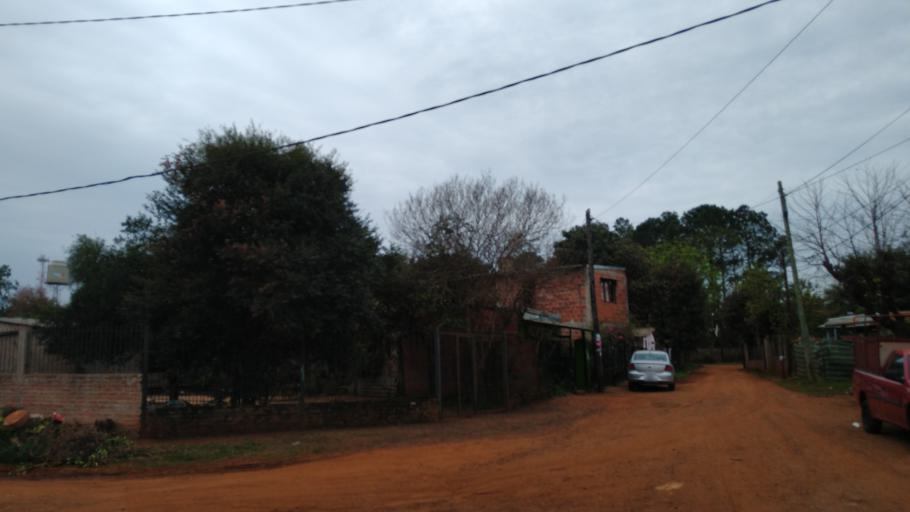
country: AR
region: Misiones
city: Garupa
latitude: -27.4381
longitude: -55.8857
